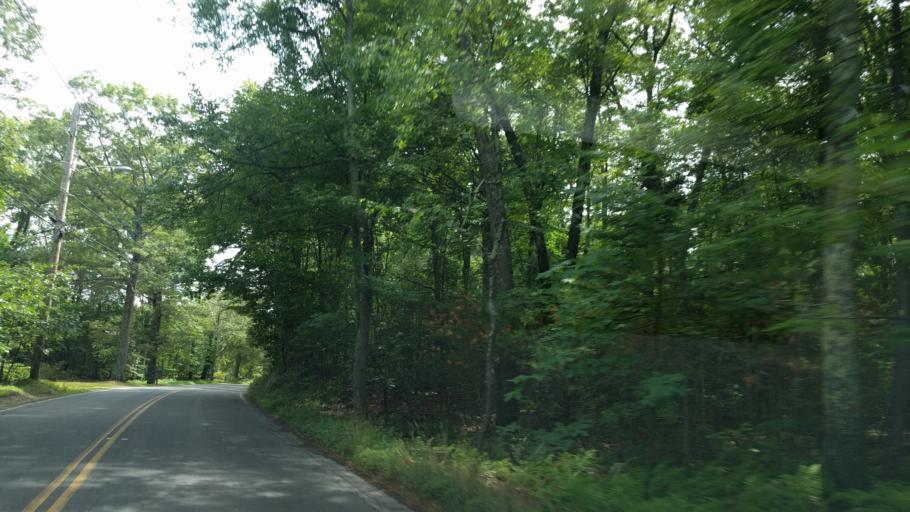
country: US
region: Massachusetts
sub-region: Worcester County
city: Whitinsville
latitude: 42.0992
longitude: -71.6922
